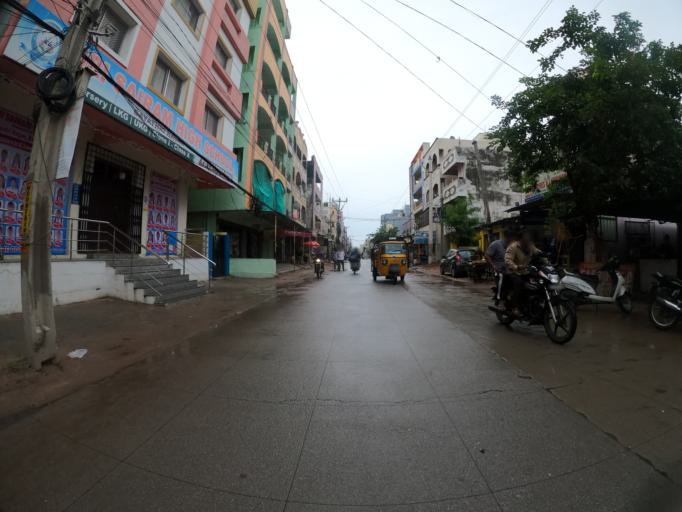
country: IN
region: Telangana
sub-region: Rangareddi
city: Kukatpalli
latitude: 17.4591
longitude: 78.4015
